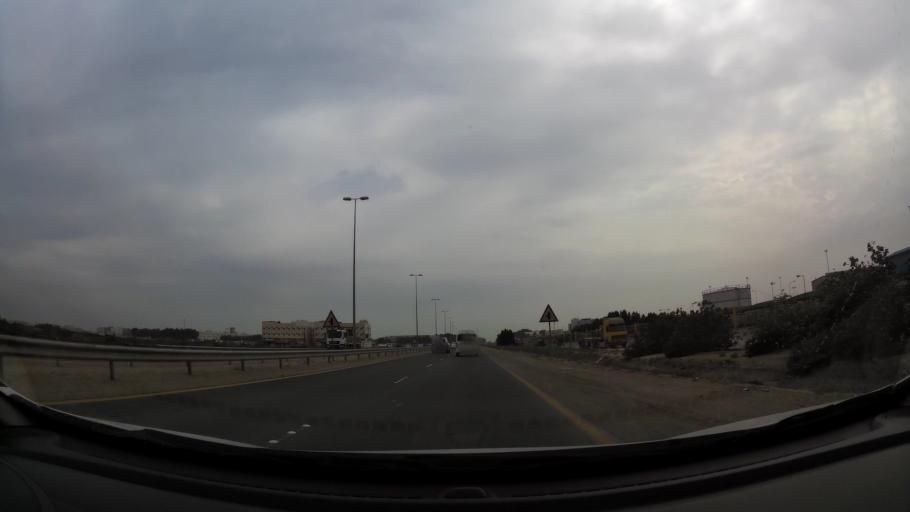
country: BH
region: Northern
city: Sitrah
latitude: 26.0883
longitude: 50.6105
